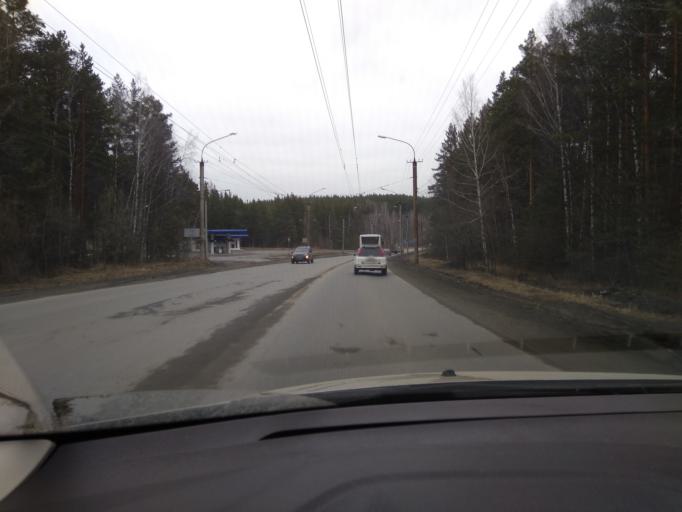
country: RU
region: Chelyabinsk
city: Turgoyak
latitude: 55.1270
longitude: 60.1350
